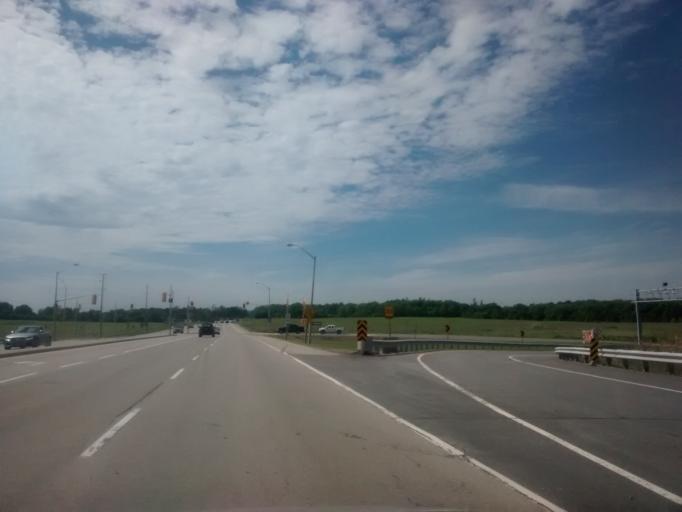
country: CA
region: Ontario
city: Burlington
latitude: 43.4159
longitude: -79.8208
